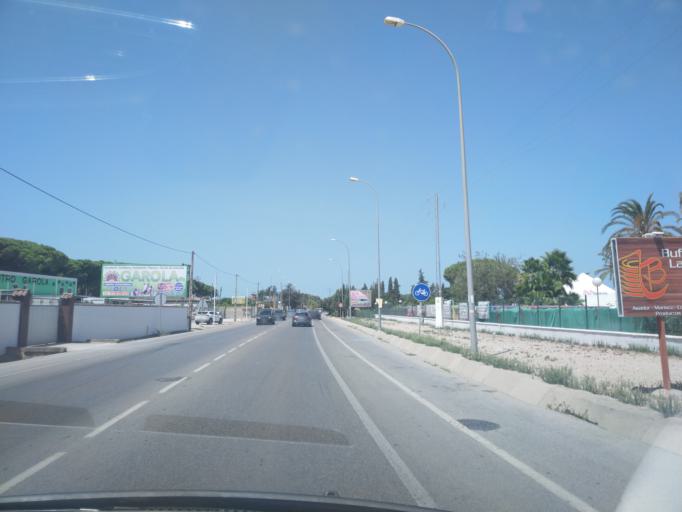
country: ES
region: Andalusia
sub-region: Provincia de Cadiz
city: Chiclana de la Frontera
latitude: 36.3945
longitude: -6.1567
